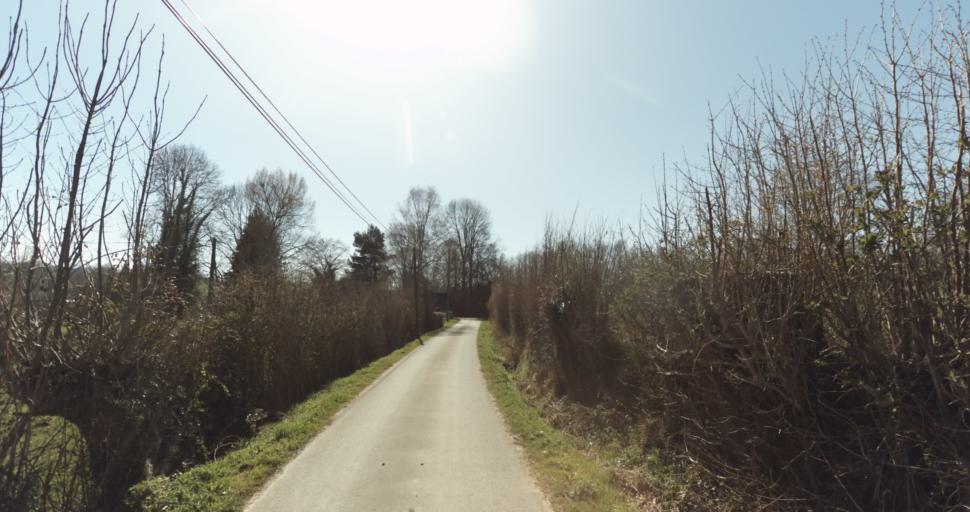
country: FR
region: Lower Normandy
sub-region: Departement du Calvados
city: Livarot
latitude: 49.0021
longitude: 0.0906
